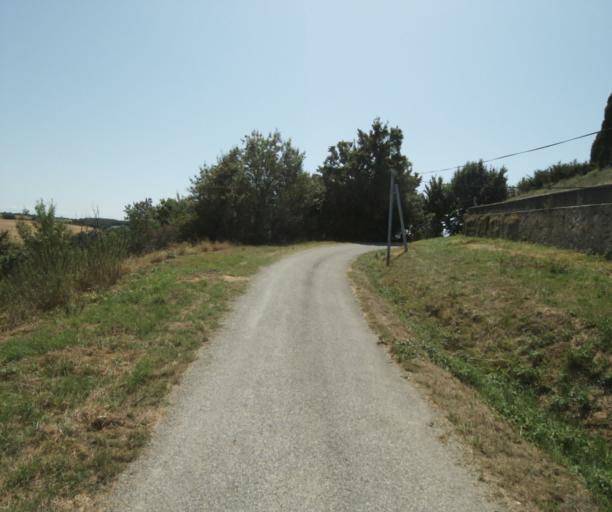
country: FR
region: Midi-Pyrenees
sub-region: Departement de la Haute-Garonne
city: Saint-Felix-Lauragais
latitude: 43.4552
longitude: 1.8384
